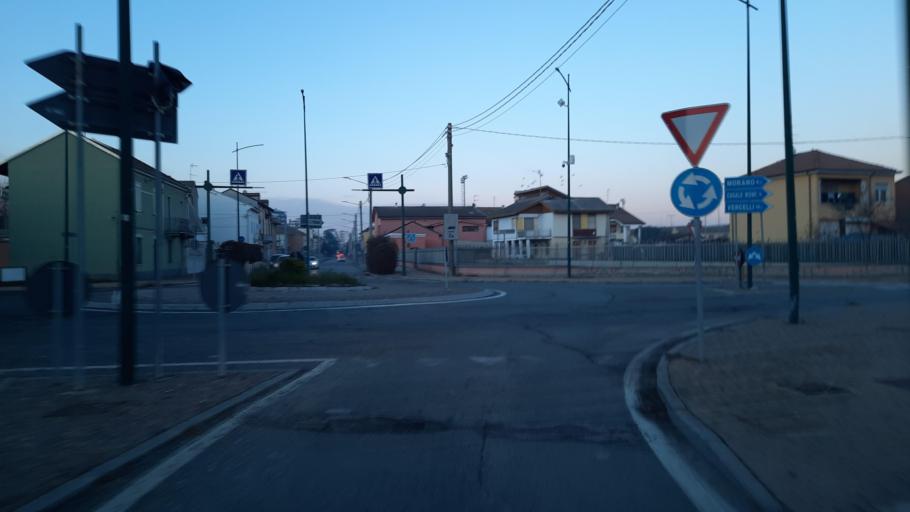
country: IT
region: Piedmont
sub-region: Provincia di Vercelli
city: Trino
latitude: 45.1872
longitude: 8.2961
